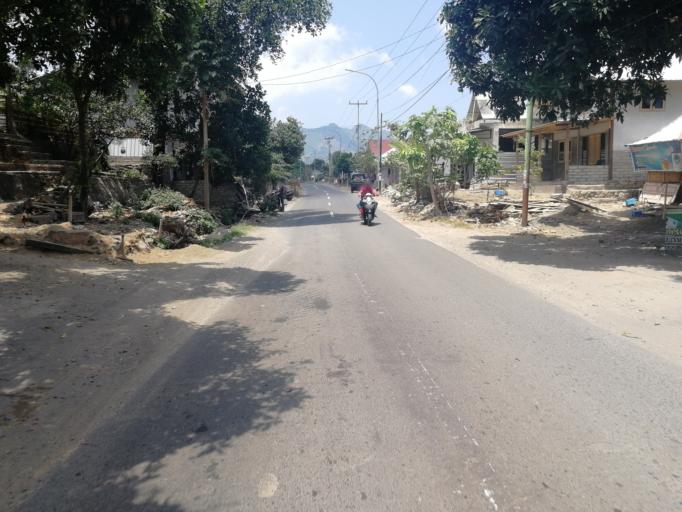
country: ID
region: West Nusa Tenggara
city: Karangsubagan
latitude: -8.4241
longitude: 116.0925
